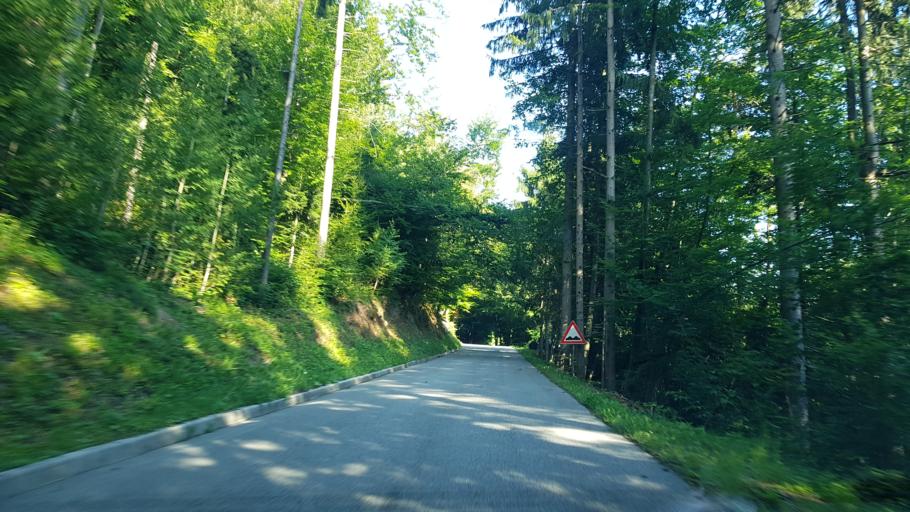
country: SI
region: Idrija
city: Spodnja Idrija
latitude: 46.0742
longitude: 14.0105
